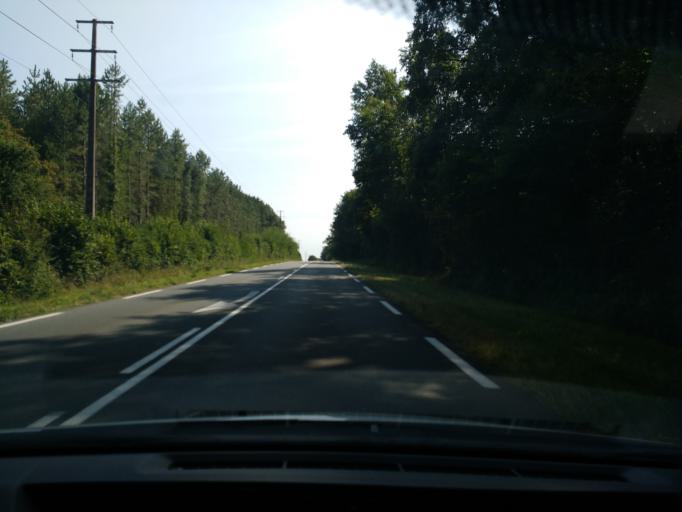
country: FR
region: Pays de la Loire
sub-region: Departement de Maine-et-Loire
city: Bauge-en-Anjou
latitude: 47.5327
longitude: -0.0608
